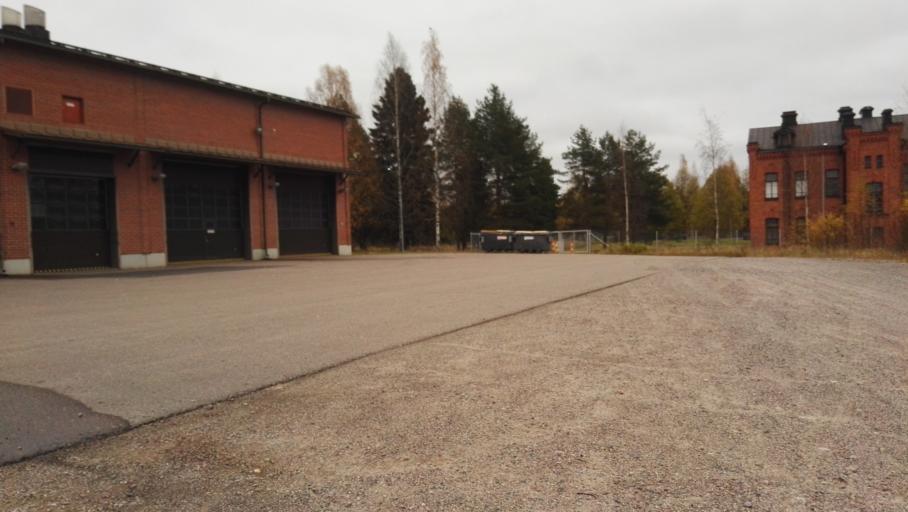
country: FI
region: Paijanne Tavastia
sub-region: Lahti
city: Lahti
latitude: 60.9644
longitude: 25.6214
